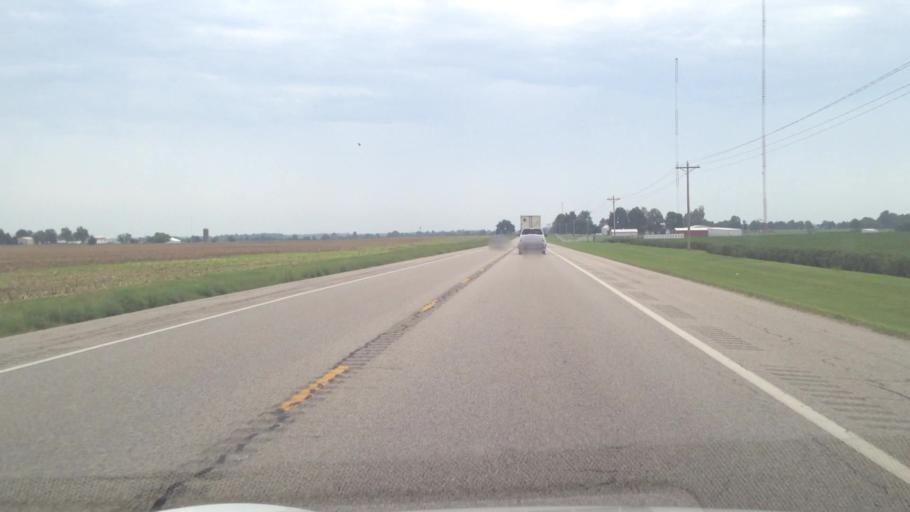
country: US
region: Missouri
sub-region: Jasper County
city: Carl Junction
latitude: 37.2287
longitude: -94.7050
